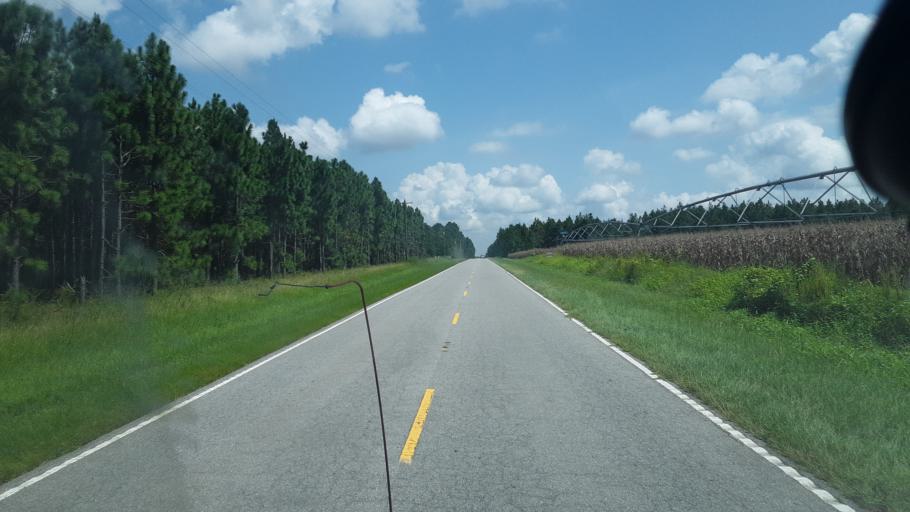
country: US
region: South Carolina
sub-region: Calhoun County
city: Oak Grove
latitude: 33.6548
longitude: -80.9836
